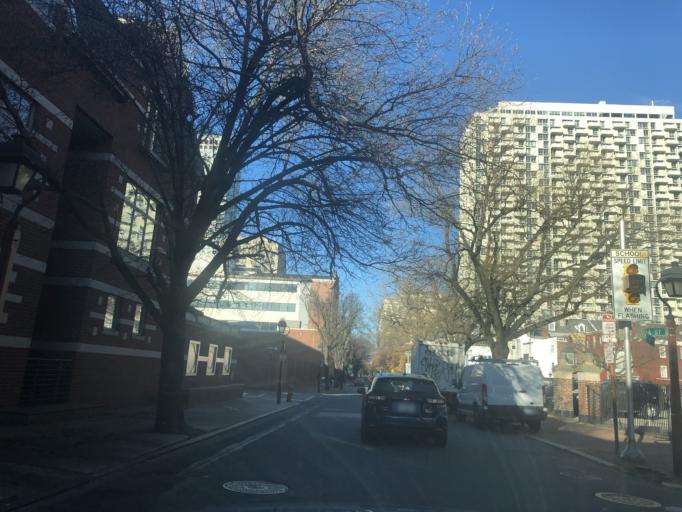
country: US
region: Pennsylvania
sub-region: Philadelphia County
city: Philadelphia
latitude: 39.9443
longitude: -75.1535
